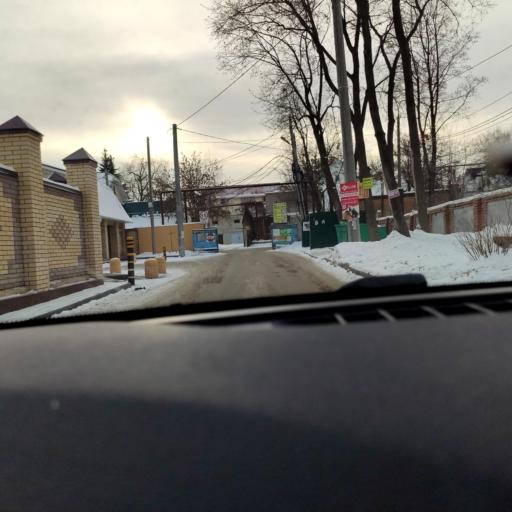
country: RU
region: Samara
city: Samara
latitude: 53.2553
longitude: 50.1836
